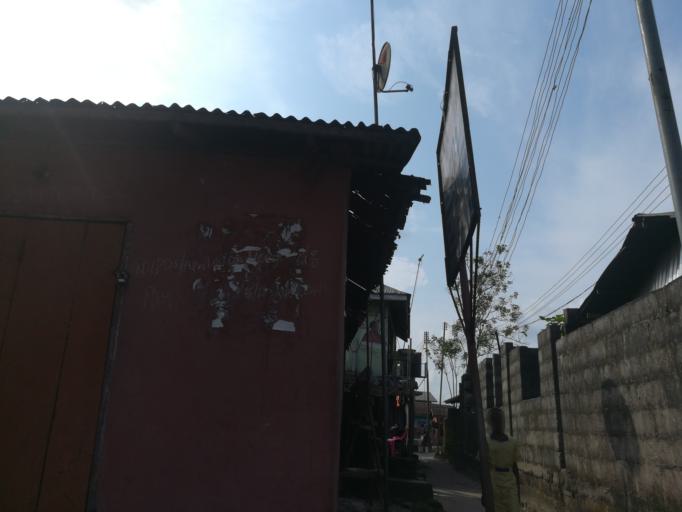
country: NG
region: Rivers
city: Okrika
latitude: 4.7424
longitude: 7.0812
